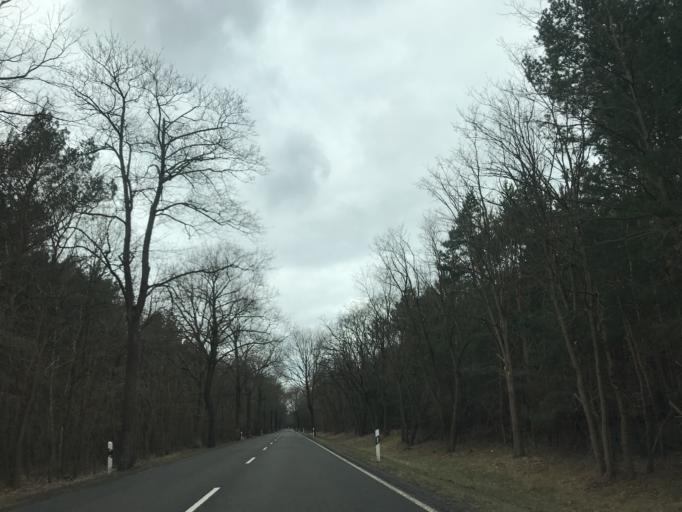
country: DE
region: Brandenburg
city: Golssen
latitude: 51.9732
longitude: 13.6585
